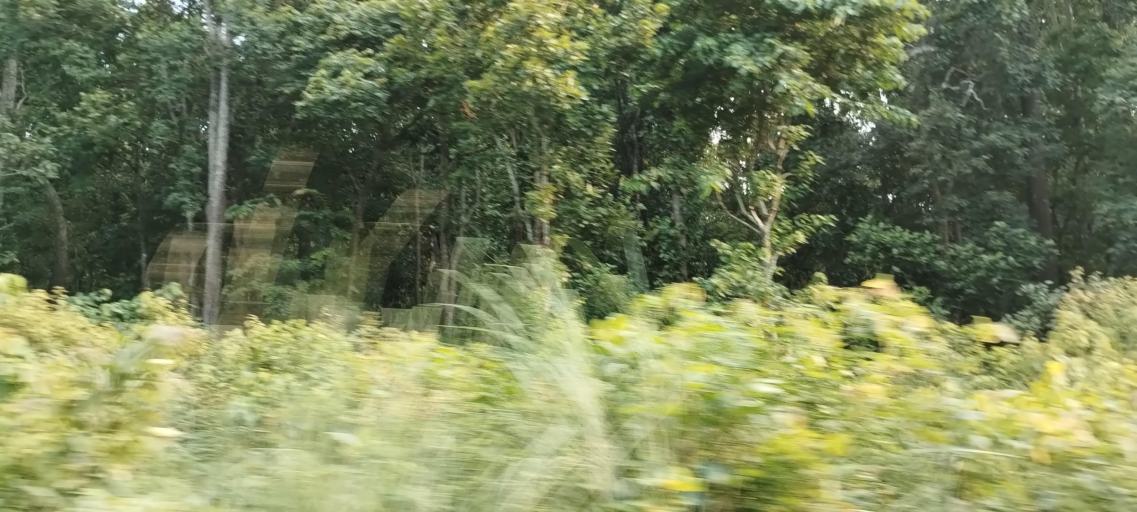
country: NP
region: Mid Western
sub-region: Bheri Zone
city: Bardiya
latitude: 28.4303
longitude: 81.3535
